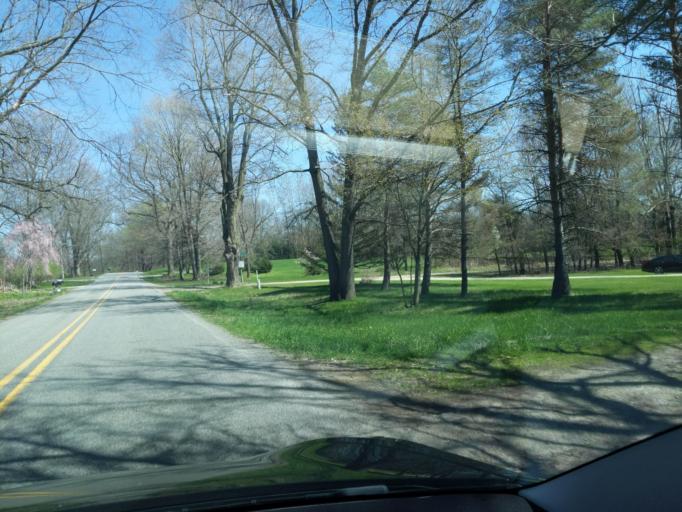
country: US
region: Michigan
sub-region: Ingham County
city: Stockbridge
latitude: 42.4868
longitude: -84.1760
